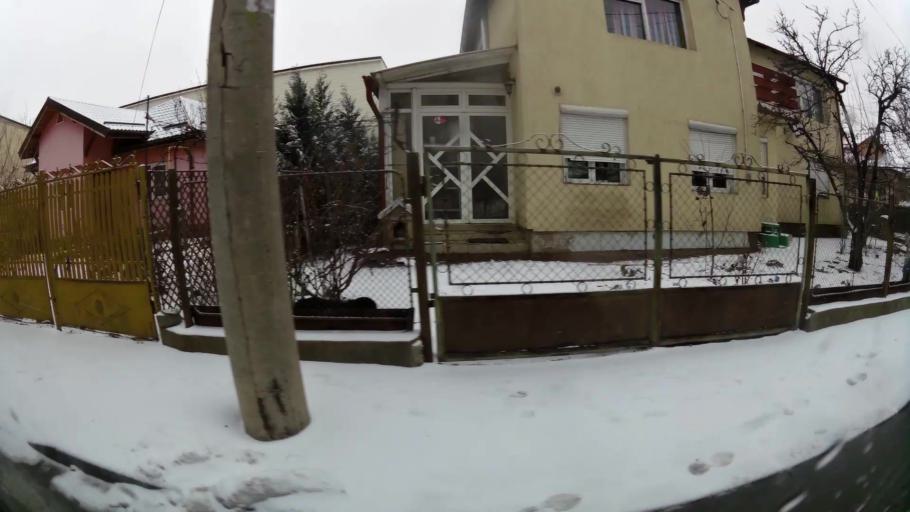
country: RO
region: Prahova
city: Ploiesti
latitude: 44.9332
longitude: 26.0153
